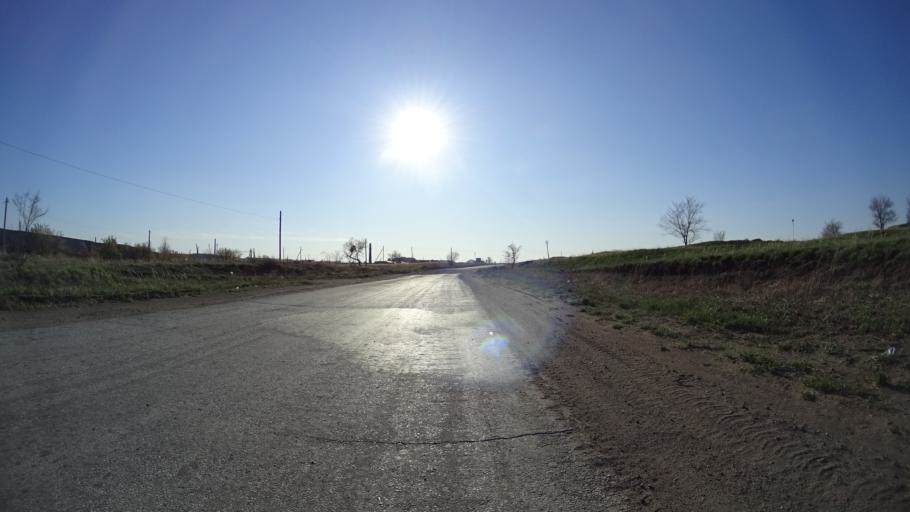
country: RU
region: Chelyabinsk
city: Troitsk
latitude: 54.0767
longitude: 61.6040
